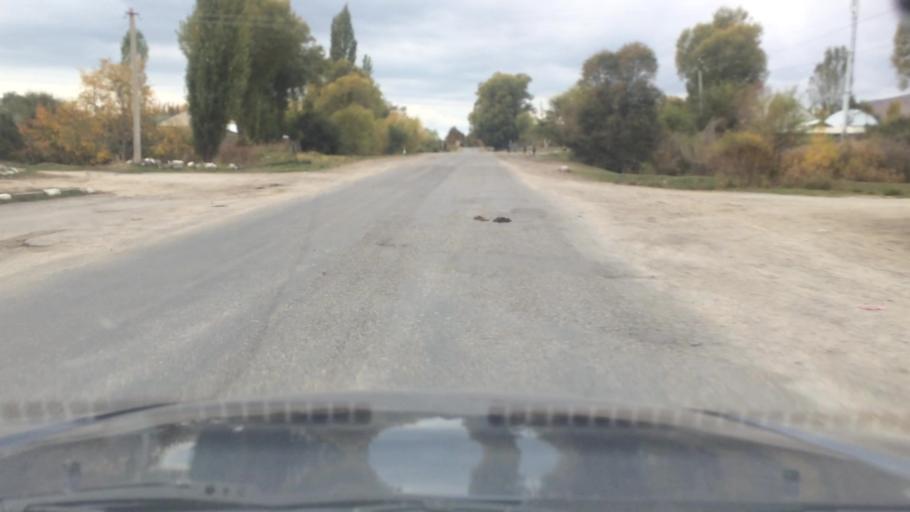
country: KG
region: Ysyk-Koel
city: Tyup
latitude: 42.7683
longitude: 78.1860
